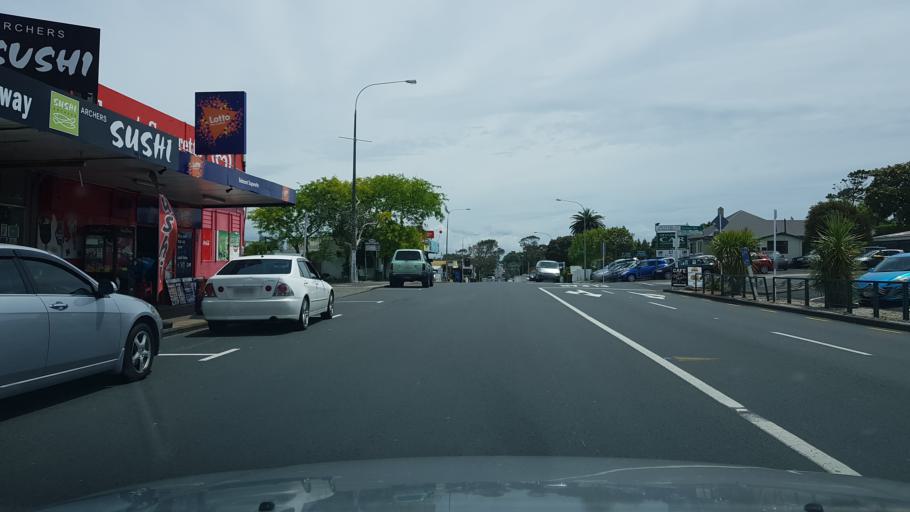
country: NZ
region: Auckland
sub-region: Auckland
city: North Shore
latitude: -36.8080
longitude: 174.7899
